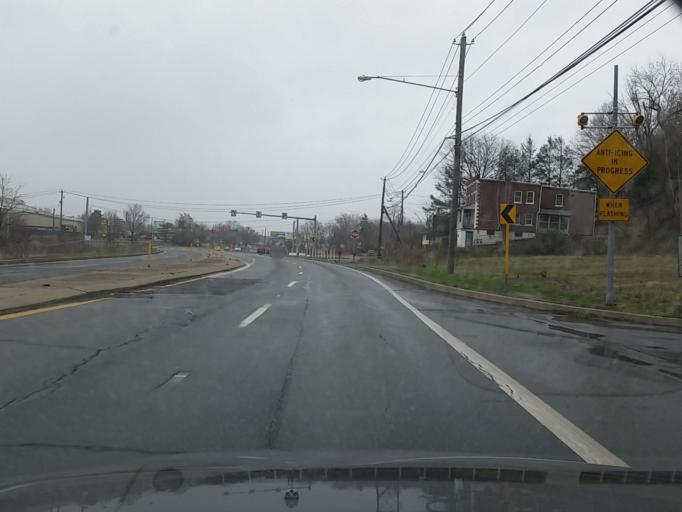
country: US
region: Pennsylvania
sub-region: Luzerne County
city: Larksville
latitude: 41.2271
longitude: -75.9285
